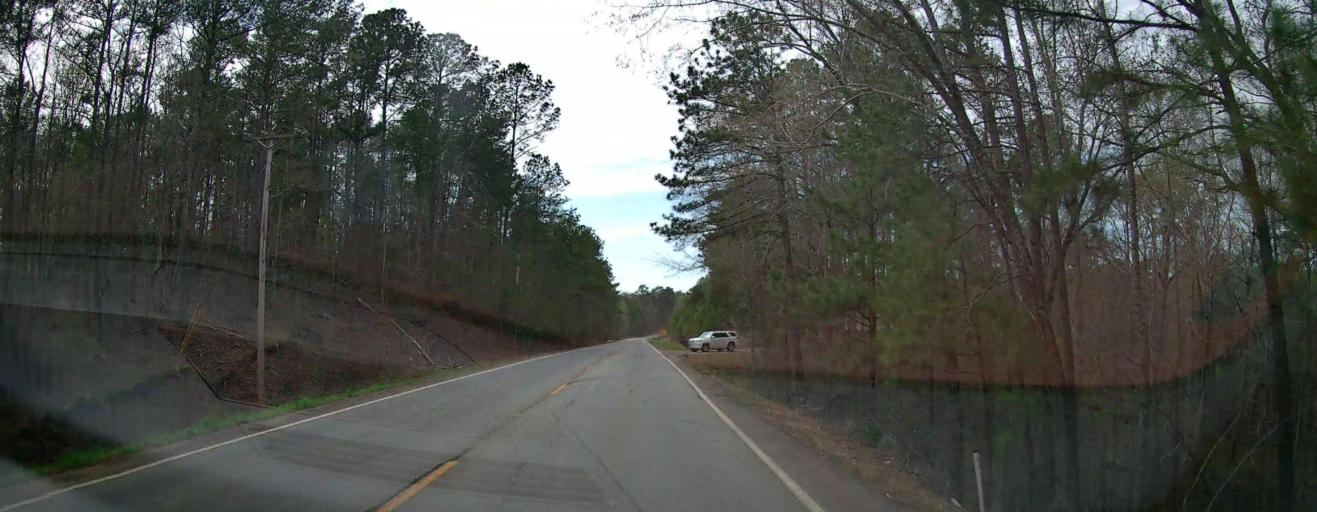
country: US
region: Georgia
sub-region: Jones County
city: Gray
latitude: 32.9868
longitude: -83.6795
